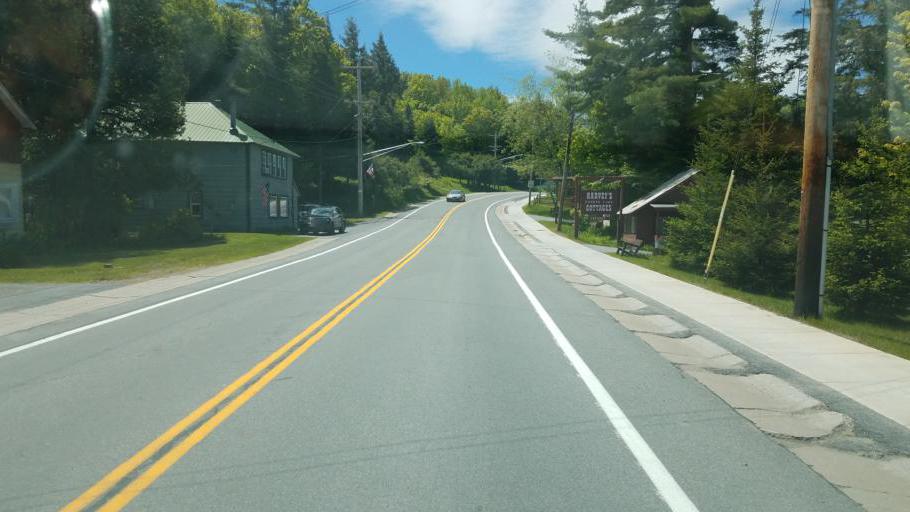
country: US
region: New York
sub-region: Hamilton County
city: Lake Pleasant
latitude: 43.7553
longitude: -74.7916
